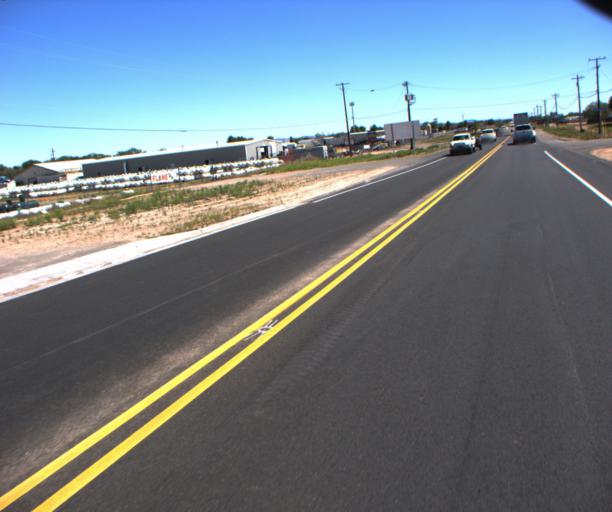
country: US
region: Arizona
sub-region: Yavapai County
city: Chino Valley
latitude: 34.7877
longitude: -112.4521
